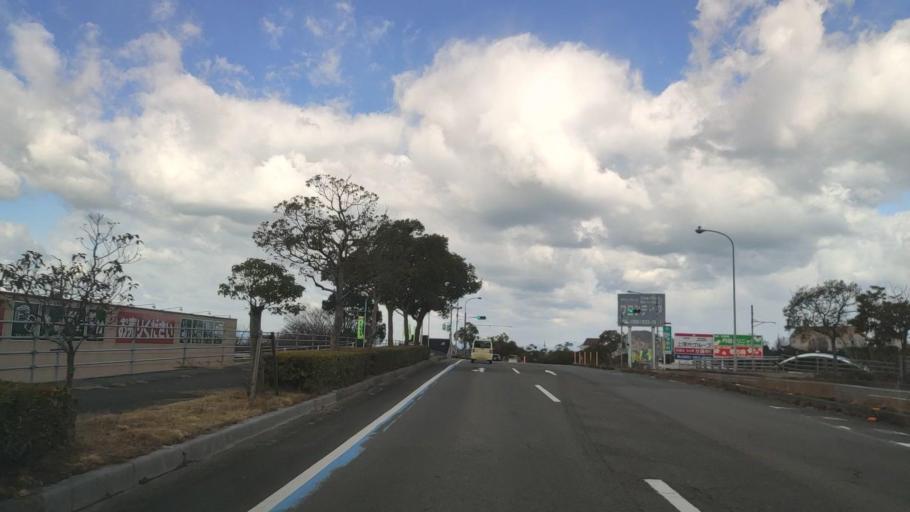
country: JP
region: Ehime
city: Hojo
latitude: 33.9468
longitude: 132.7754
